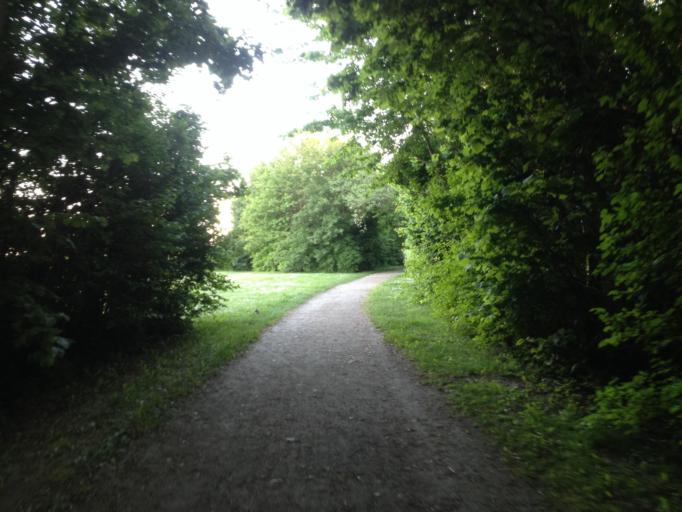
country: SE
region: Skane
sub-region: Lunds Kommun
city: Lund
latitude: 55.7074
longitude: 13.2467
